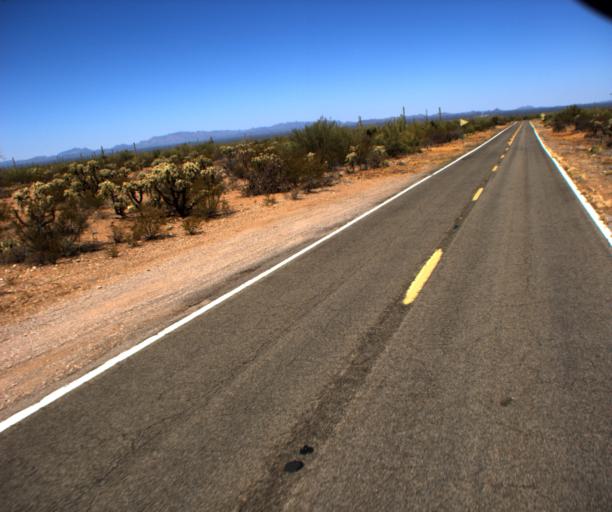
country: US
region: Arizona
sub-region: Pima County
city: Sells
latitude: 32.1774
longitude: -112.2683
